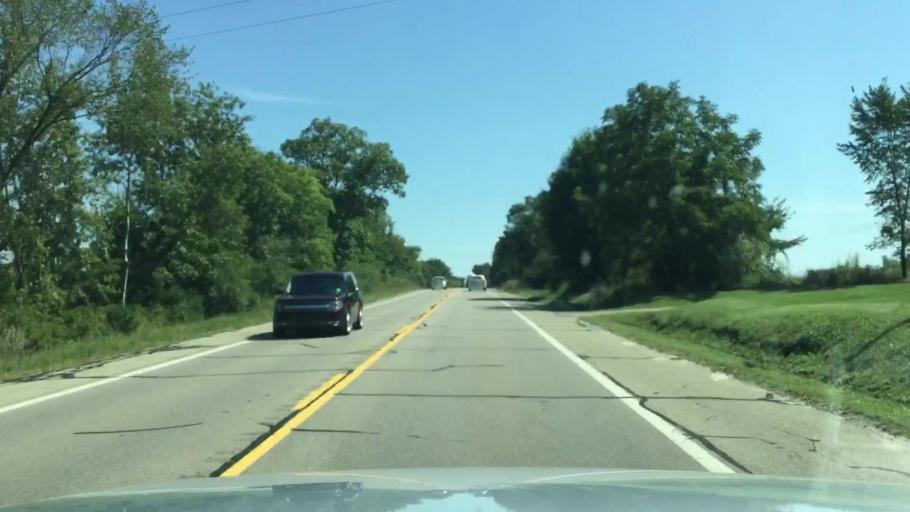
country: US
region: Michigan
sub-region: Washtenaw County
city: Manchester
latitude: 42.0728
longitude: -84.0530
